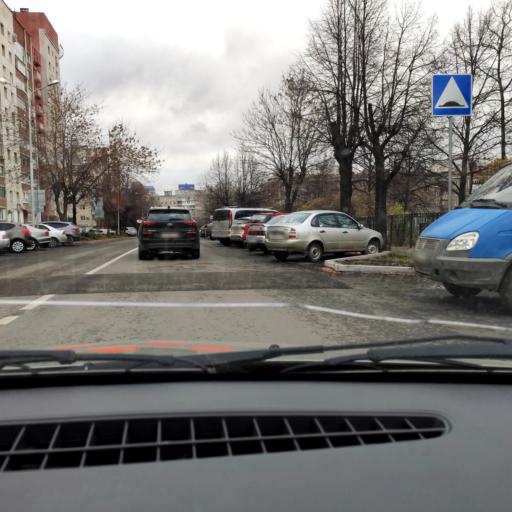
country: RU
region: Bashkortostan
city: Ufa
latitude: 54.7299
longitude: 55.9734
